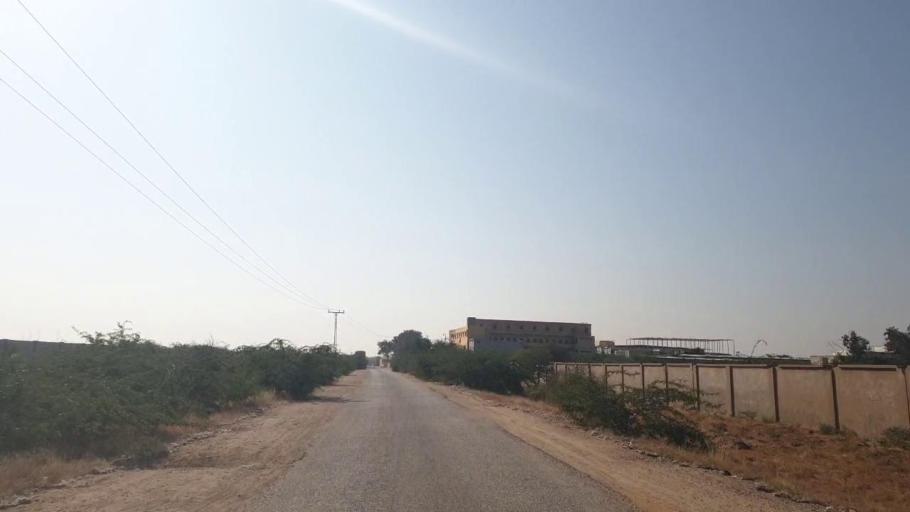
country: PK
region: Sindh
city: Thatta
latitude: 25.1571
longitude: 67.7735
